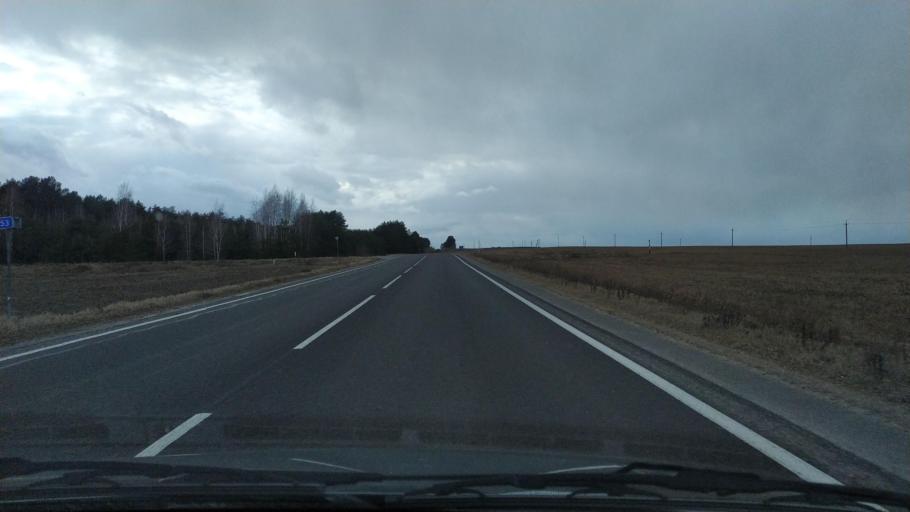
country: BY
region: Brest
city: Kamyanyets
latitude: 52.4009
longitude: 23.8799
